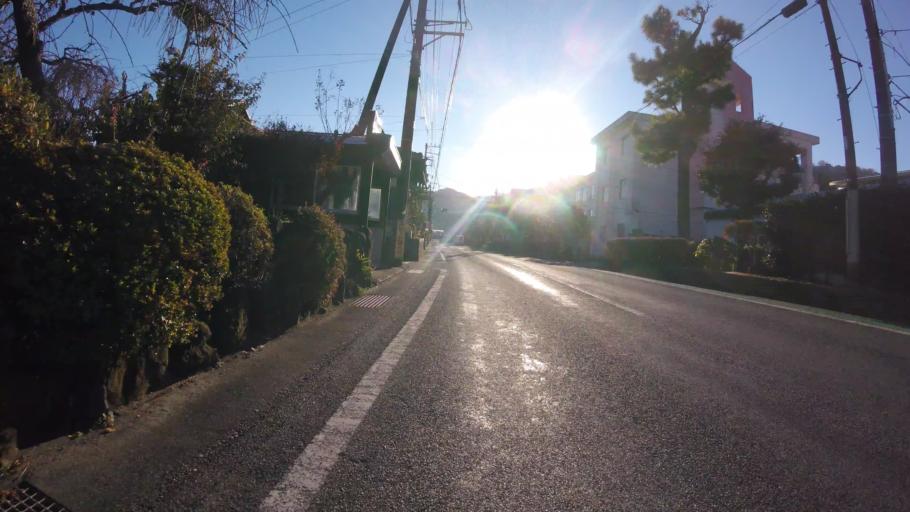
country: JP
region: Shizuoka
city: Numazu
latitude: 34.9910
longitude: 138.9302
